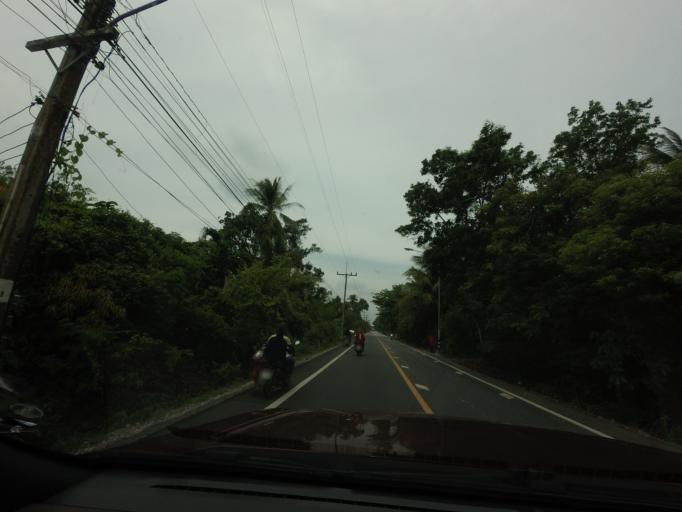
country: TH
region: Pattani
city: Yaring
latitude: 6.8559
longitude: 101.3614
